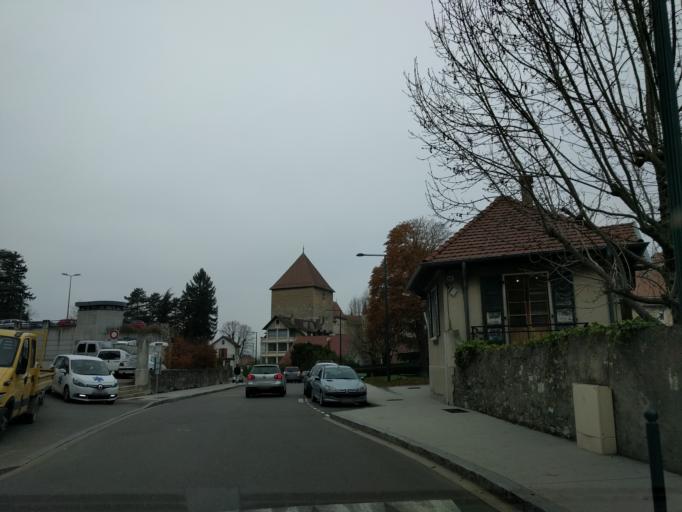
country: FR
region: Rhone-Alpes
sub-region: Departement de la Haute-Savoie
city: Annecy
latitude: 45.8963
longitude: 6.1273
